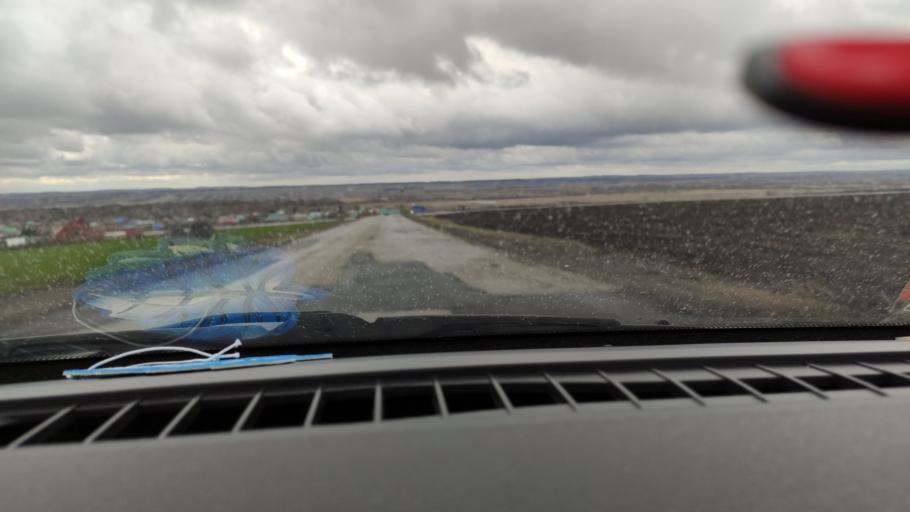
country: RU
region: Tatarstan
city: Nurlat
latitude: 54.3987
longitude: 50.7828
